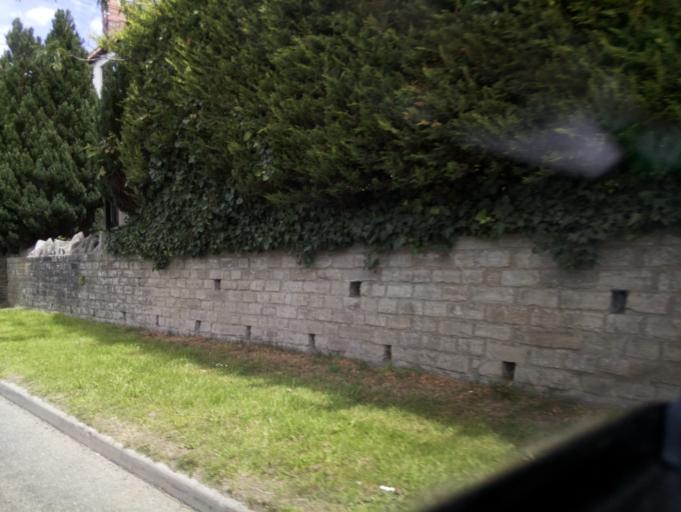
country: GB
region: England
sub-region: Somerset
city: Wells
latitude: 51.1897
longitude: -2.6762
